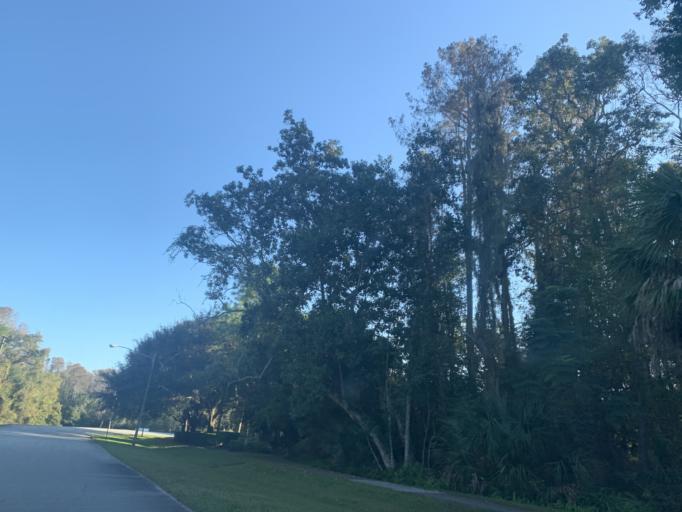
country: US
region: Florida
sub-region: Pinellas County
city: East Lake
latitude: 28.1207
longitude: -82.6908
